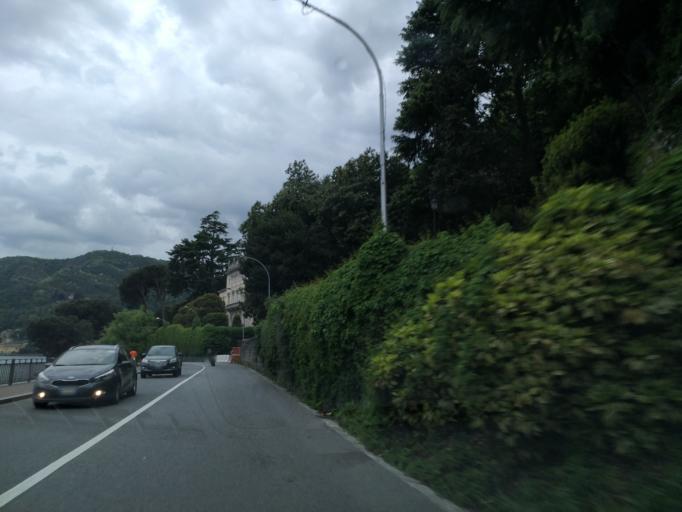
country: IT
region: Lombardy
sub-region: Provincia di Como
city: Cernobbio
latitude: 45.8241
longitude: 9.0681
